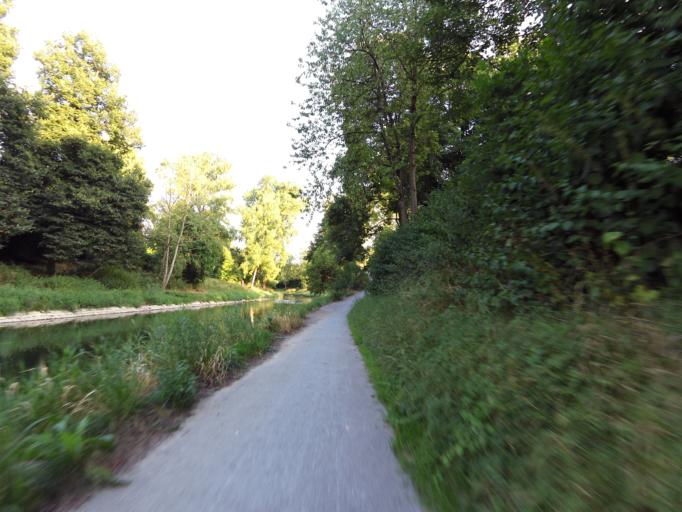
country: CH
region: Zurich
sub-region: Bezirk Buelach
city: Glattbrugg / Rohr/Platten-Balsberg
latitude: 47.4337
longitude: 8.5667
